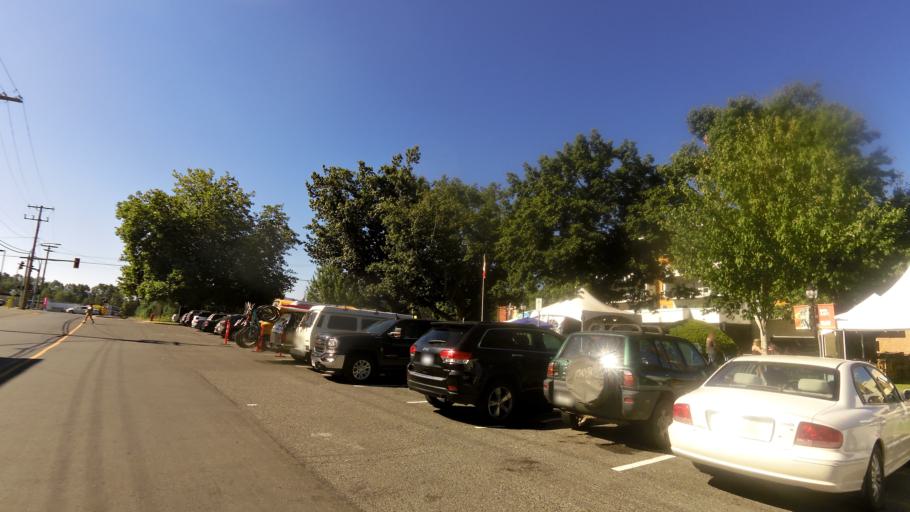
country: CA
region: British Columbia
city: Duncan
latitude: 48.7776
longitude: -123.7063
